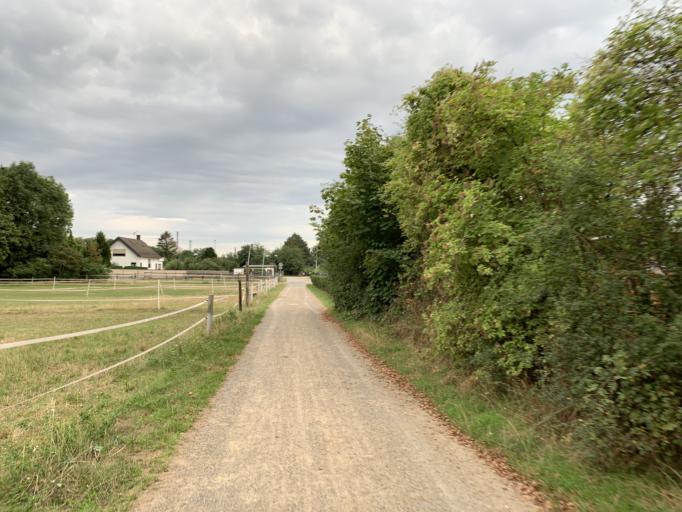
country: DE
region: North Rhine-Westphalia
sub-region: Regierungsbezirk Koln
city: Dueren
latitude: 50.7838
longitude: 6.4849
